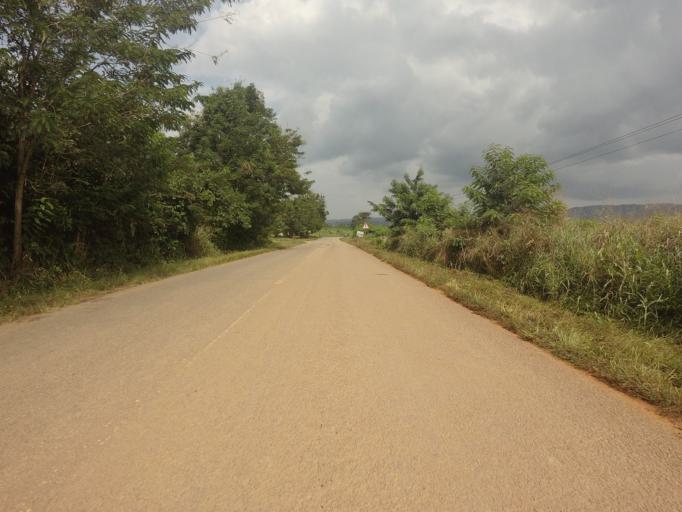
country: GH
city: Akropong
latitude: 5.9565
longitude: -0.1690
